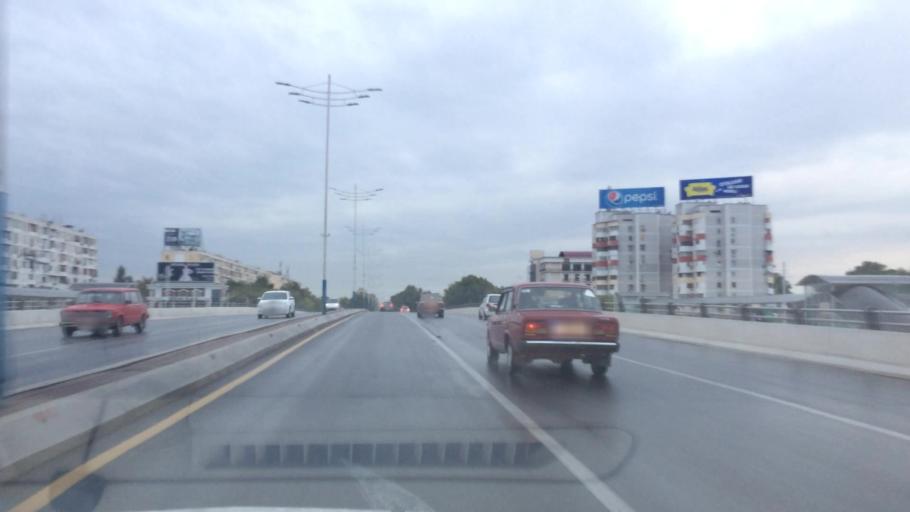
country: UZ
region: Toshkent Shahri
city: Tashkent
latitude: 41.2928
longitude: 69.2242
